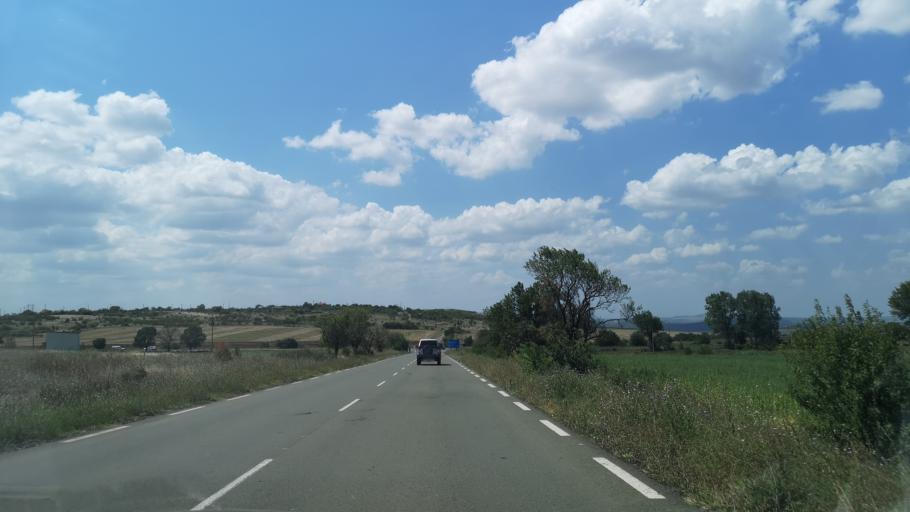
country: BG
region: Burgas
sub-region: Obshtina Kameno
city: Kameno
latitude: 42.6364
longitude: 27.3444
